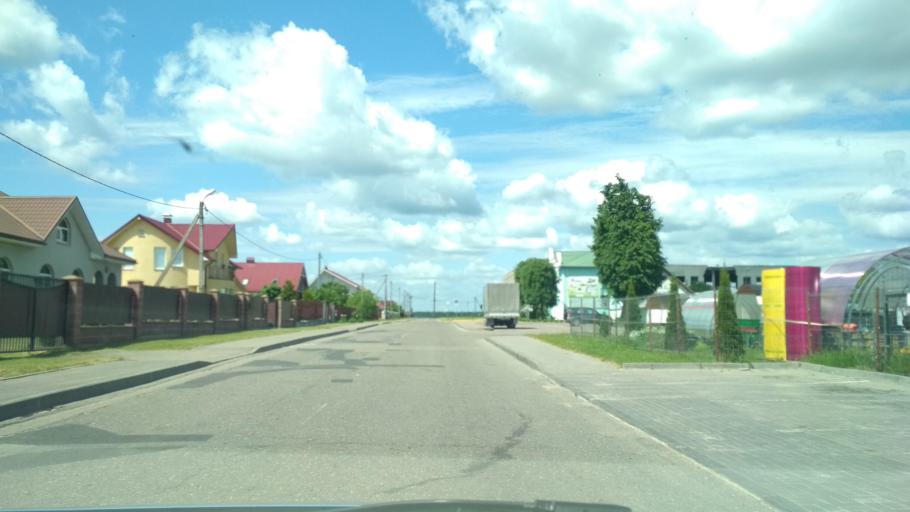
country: BY
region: Grodnenskaya
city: Astravyets
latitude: 54.6215
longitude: 25.9604
